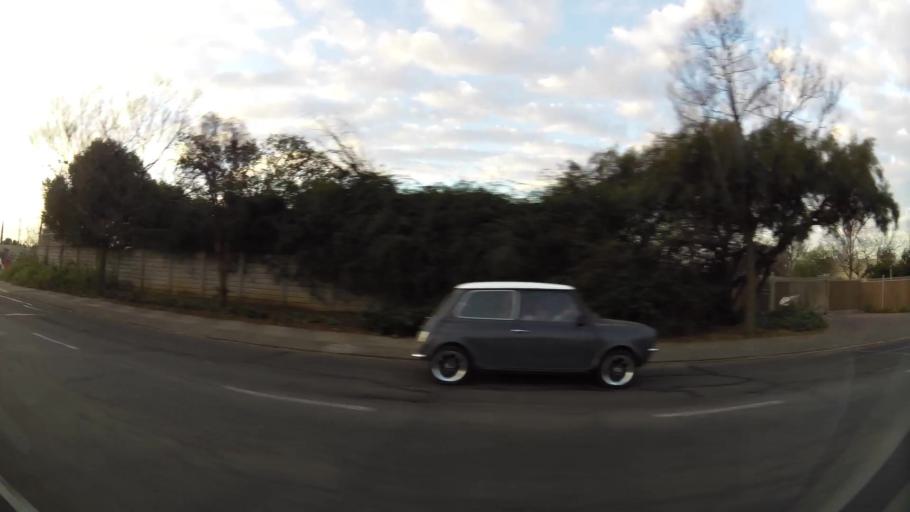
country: ZA
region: Orange Free State
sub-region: Mangaung Metropolitan Municipality
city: Bloemfontein
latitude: -29.1543
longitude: 26.1842
